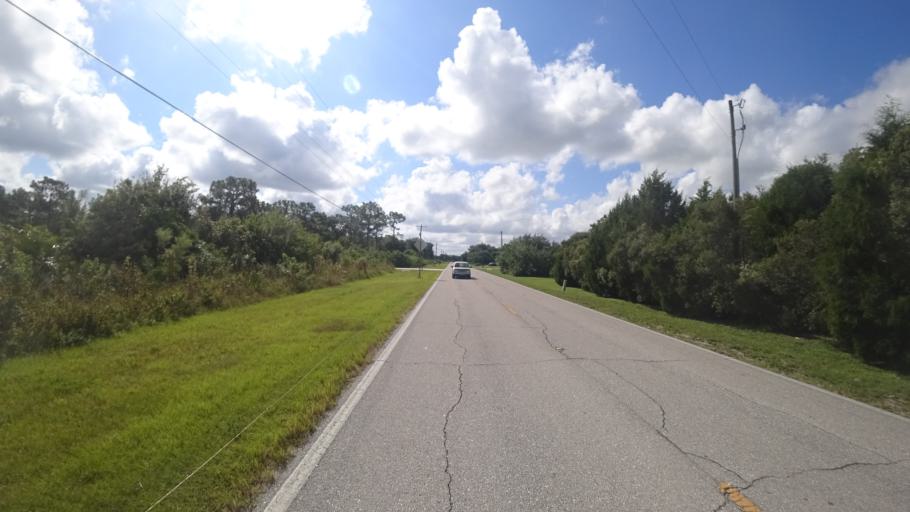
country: US
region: Florida
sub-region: Sarasota County
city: Lake Sarasota
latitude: 27.3916
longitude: -82.2712
